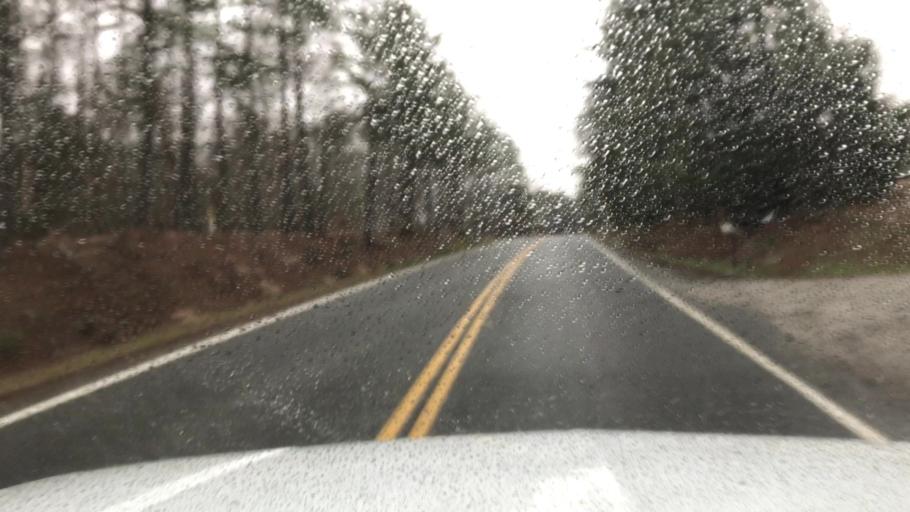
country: US
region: Virginia
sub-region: Henrico County
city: Short Pump
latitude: 37.6510
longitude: -77.6775
